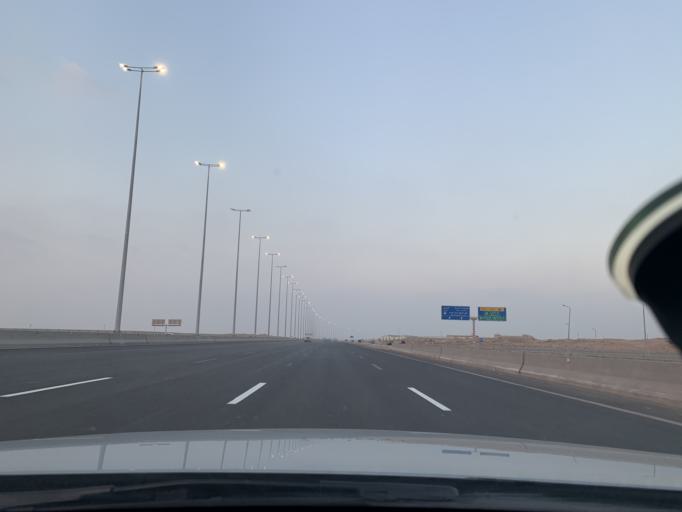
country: EG
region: Muhafazat al Qalyubiyah
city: Al Khankah
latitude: 30.0851
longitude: 31.4550
